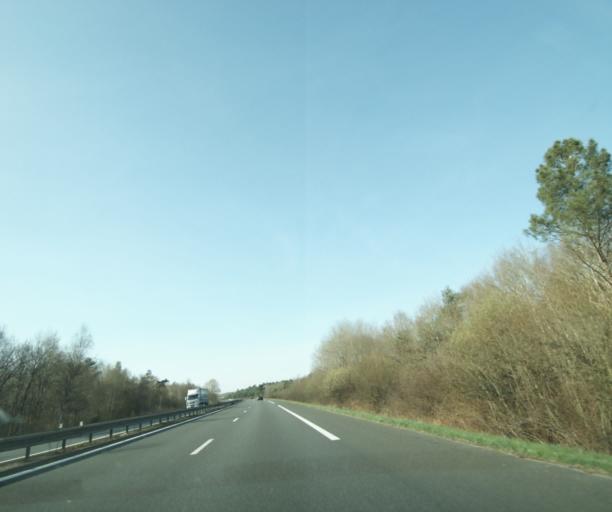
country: FR
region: Centre
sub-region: Departement du Loiret
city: La Ferte-Saint-Aubin
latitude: 47.7134
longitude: 1.8983
